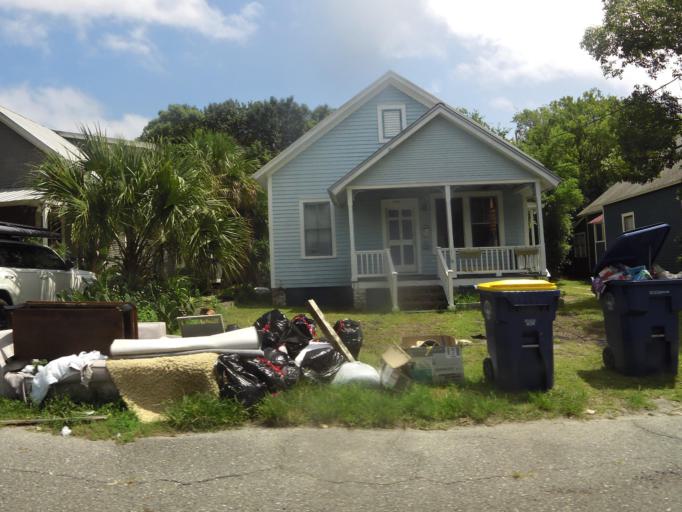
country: US
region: Florida
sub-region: Nassau County
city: Fernandina Beach
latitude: 30.6643
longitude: -81.4614
